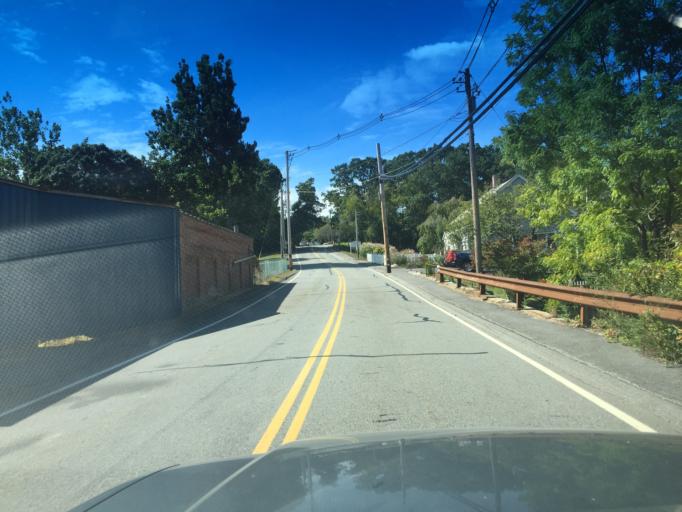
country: US
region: Massachusetts
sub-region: Worcester County
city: Northborough
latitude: 42.3231
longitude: -71.6392
